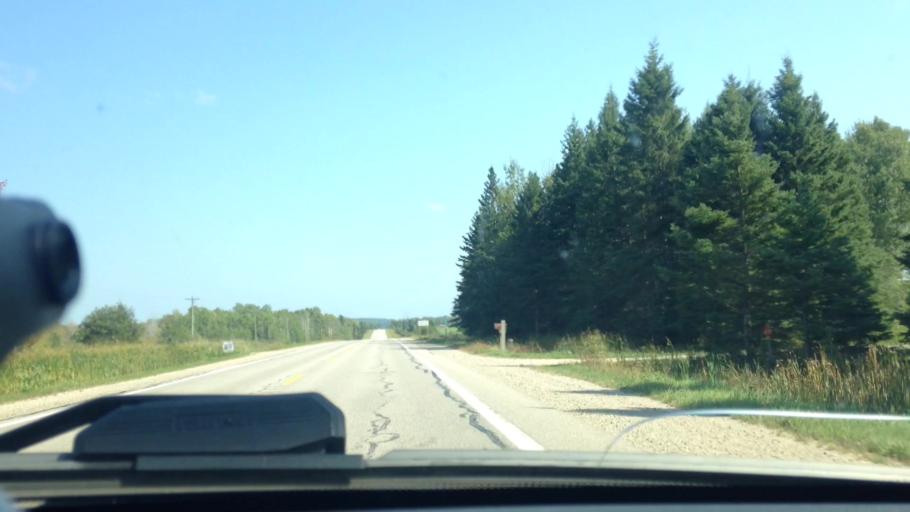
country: US
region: Michigan
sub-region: Luce County
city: Newberry
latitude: 46.3102
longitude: -85.6139
